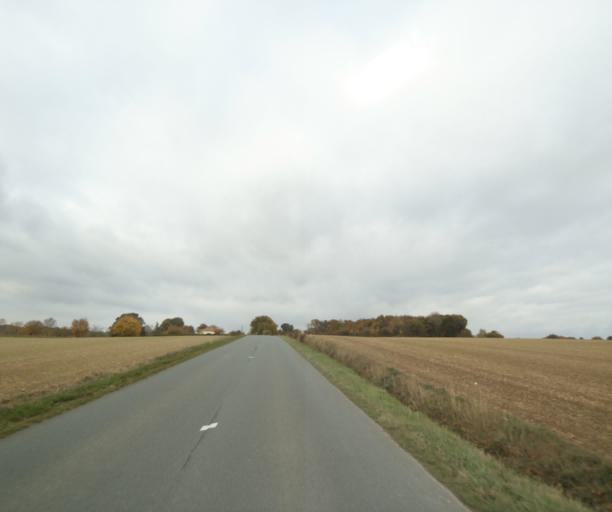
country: FR
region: Poitou-Charentes
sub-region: Departement de la Charente-Maritime
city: Saint-Georges-des-Coteaux
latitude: 45.7743
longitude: -0.7048
